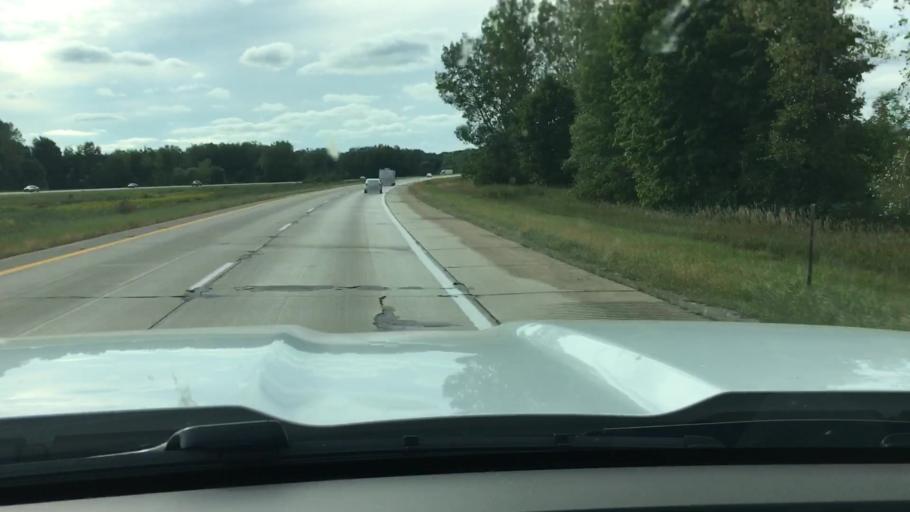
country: US
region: Michigan
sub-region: Lapeer County
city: Imlay City
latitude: 42.9967
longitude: -83.1342
